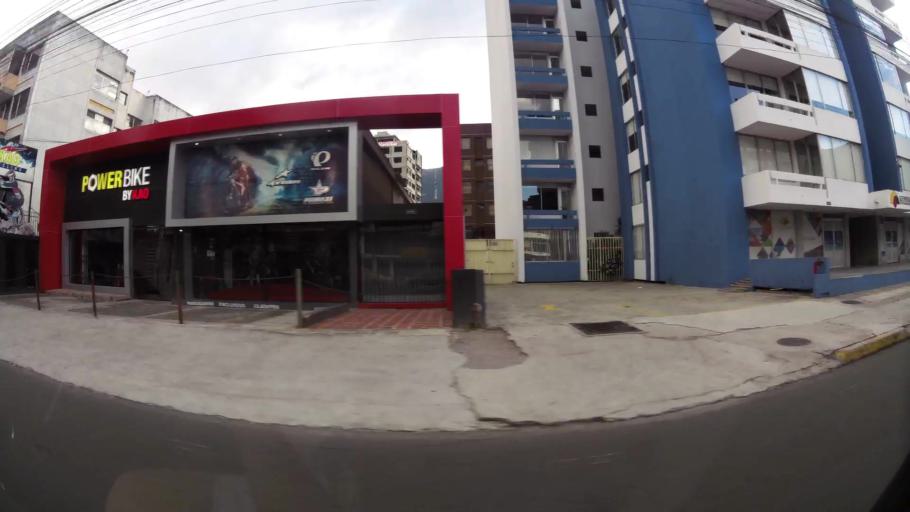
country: EC
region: Pichincha
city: Quito
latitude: -0.1907
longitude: -78.4882
